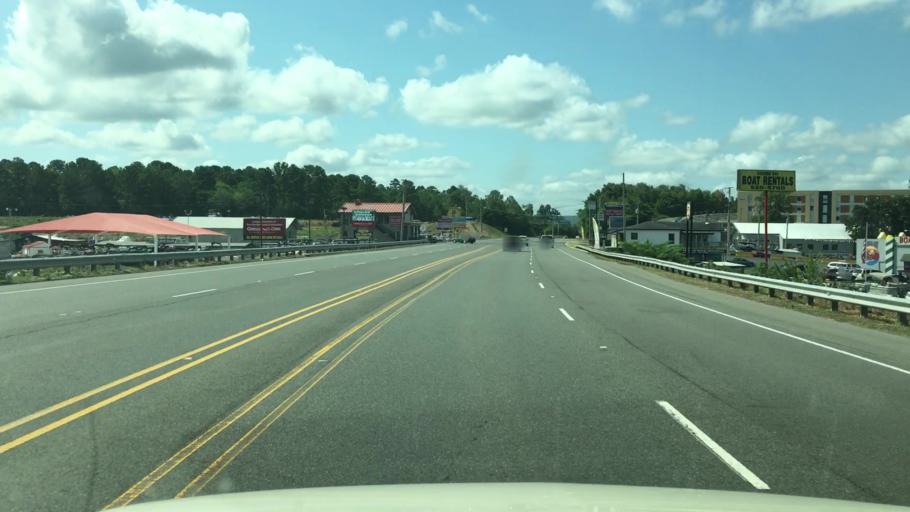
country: US
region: Arkansas
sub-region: Garland County
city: Lake Hamilton
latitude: 34.4409
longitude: -93.0886
